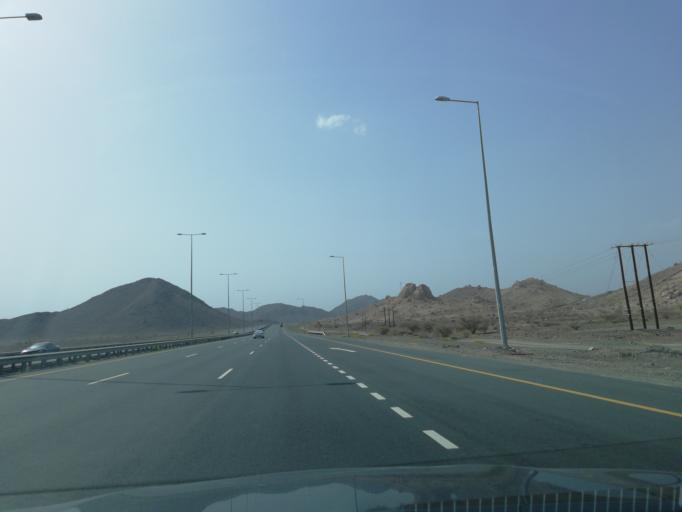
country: OM
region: Ash Sharqiyah
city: Ibra'
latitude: 22.9329
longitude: 58.2553
